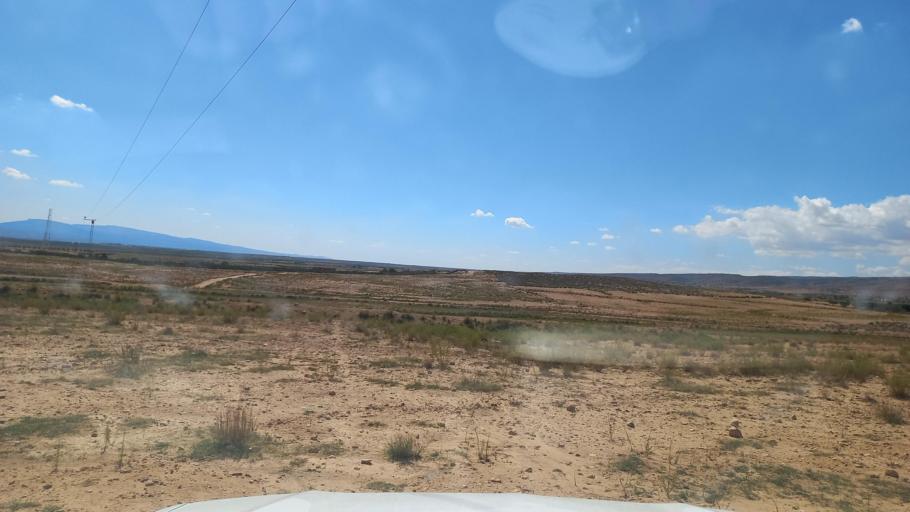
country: TN
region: Al Qasrayn
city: Sbiba
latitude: 35.3537
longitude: 9.0131
